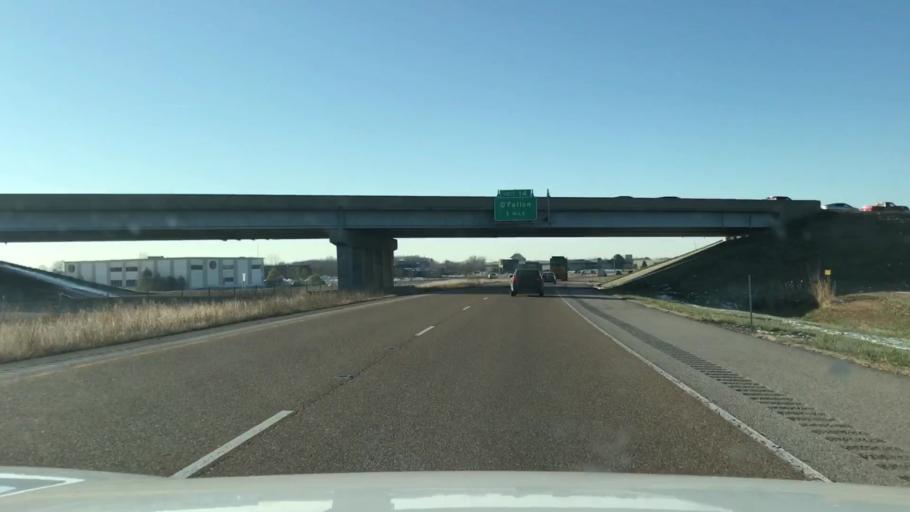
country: US
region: Illinois
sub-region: Saint Clair County
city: O'Fallon
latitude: 38.5757
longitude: -89.9285
